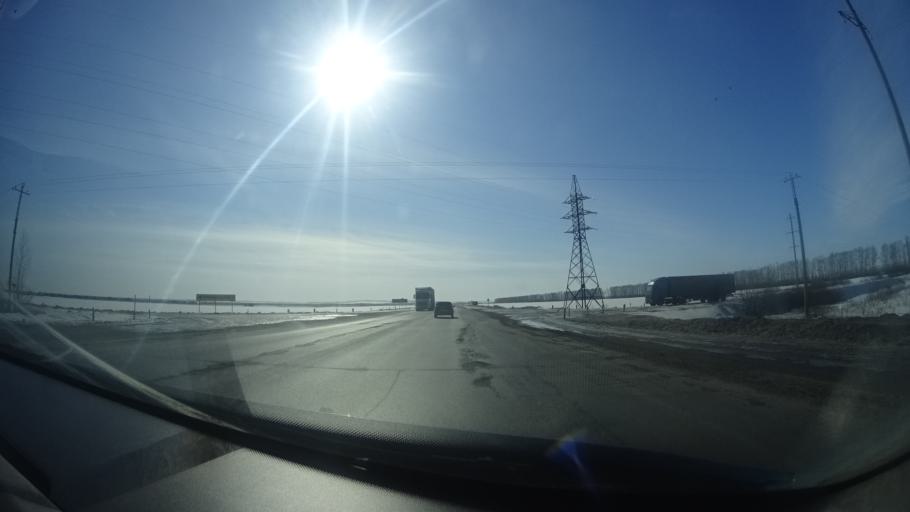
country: RU
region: Bashkortostan
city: Mikhaylovka
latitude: 54.9489
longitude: 55.7533
